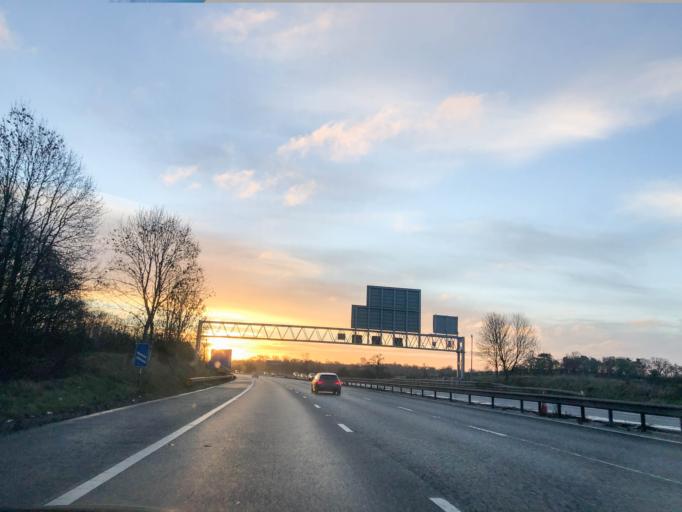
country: GB
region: England
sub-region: Warwickshire
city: Henley in Arden
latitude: 52.3386
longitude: -1.7843
